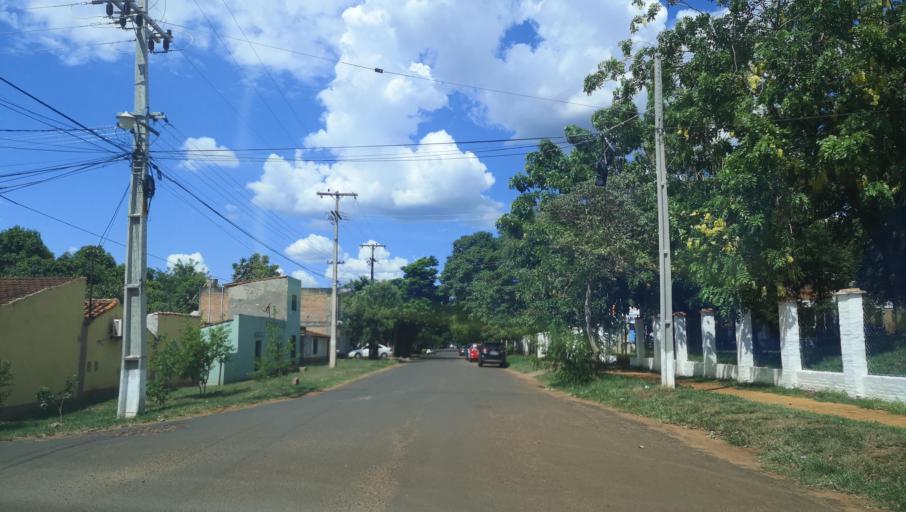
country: PY
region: Misiones
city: Santa Maria
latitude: -26.8887
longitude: -57.0337
